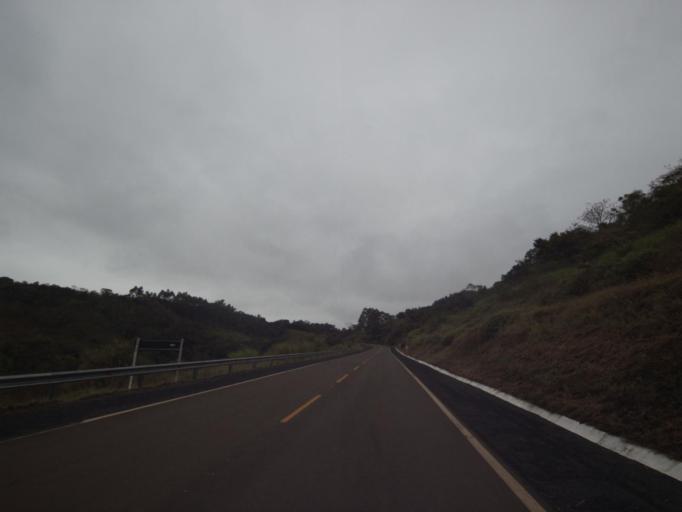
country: AR
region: Misiones
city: El Soberbio
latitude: -27.2880
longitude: -54.1811
